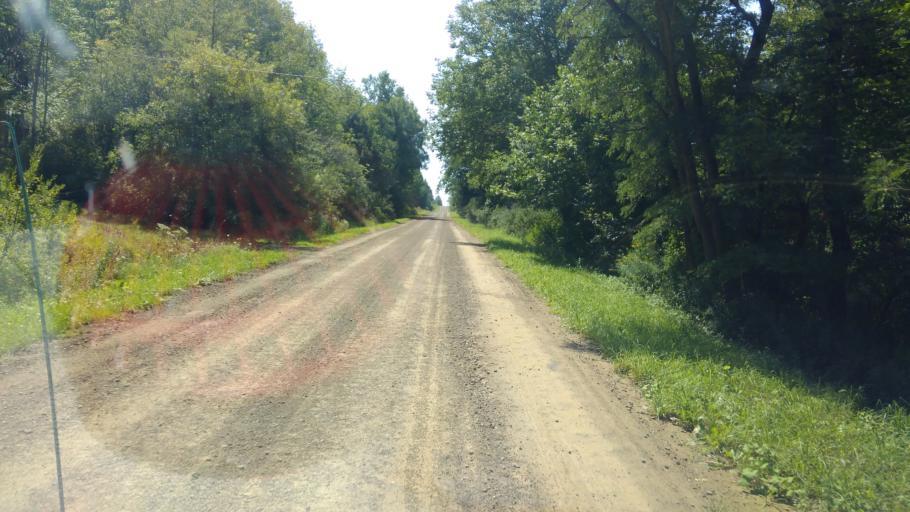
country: US
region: New York
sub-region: Allegany County
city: Houghton
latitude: 42.3624
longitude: -78.0405
